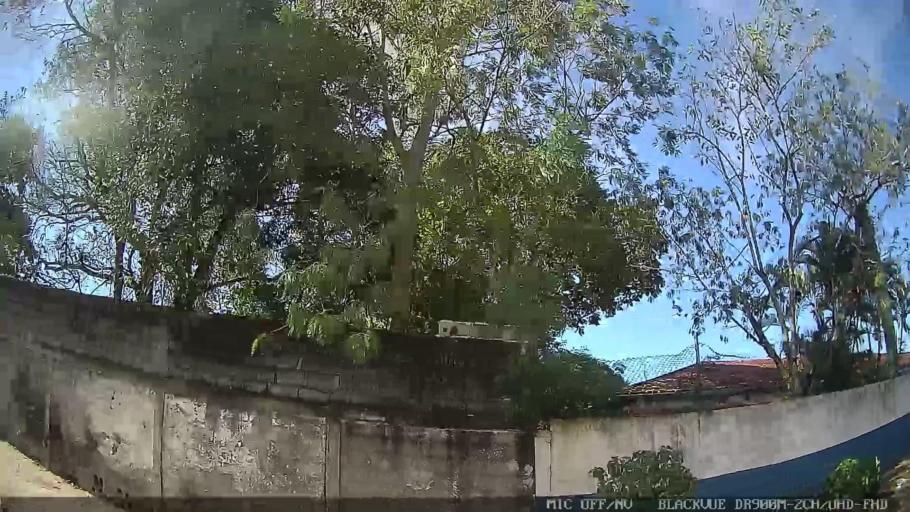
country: BR
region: Sao Paulo
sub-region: Guaruja
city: Guaruja
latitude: -23.9468
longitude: -46.2815
